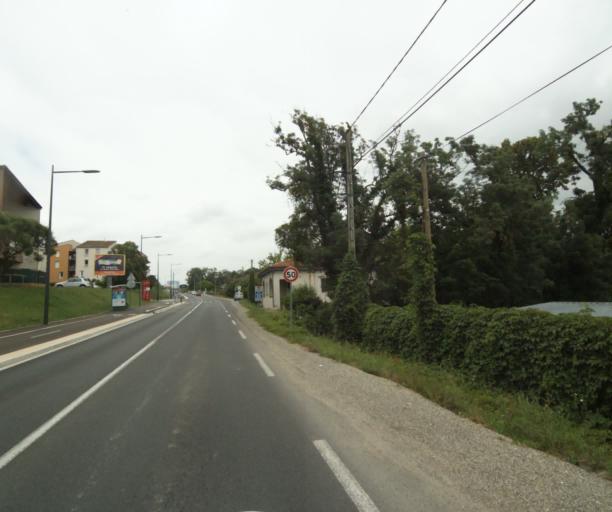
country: FR
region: Midi-Pyrenees
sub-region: Departement du Tarn-et-Garonne
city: Montauban
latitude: 44.0031
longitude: 1.3657
